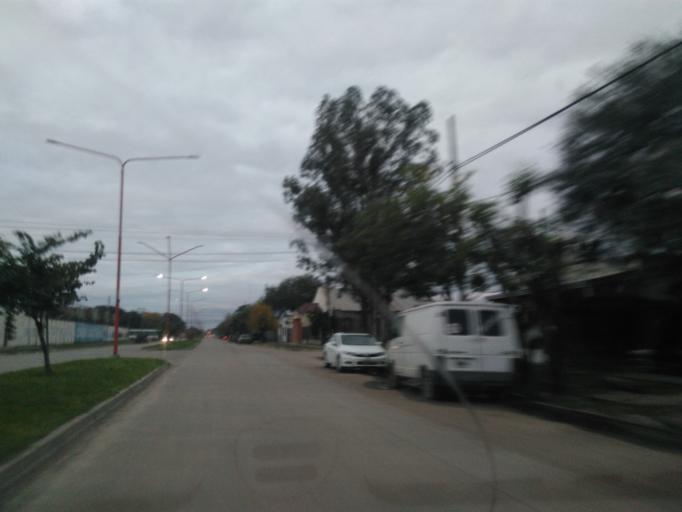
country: AR
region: Chaco
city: Resistencia
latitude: -27.4779
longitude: -58.9967
